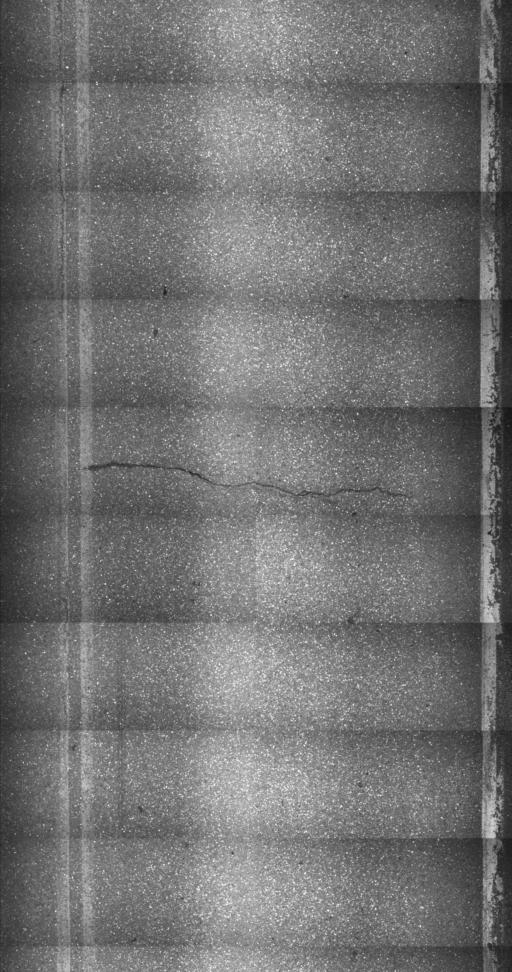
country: US
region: Vermont
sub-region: Washington County
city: Waterbury
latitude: 44.1990
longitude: -72.8943
